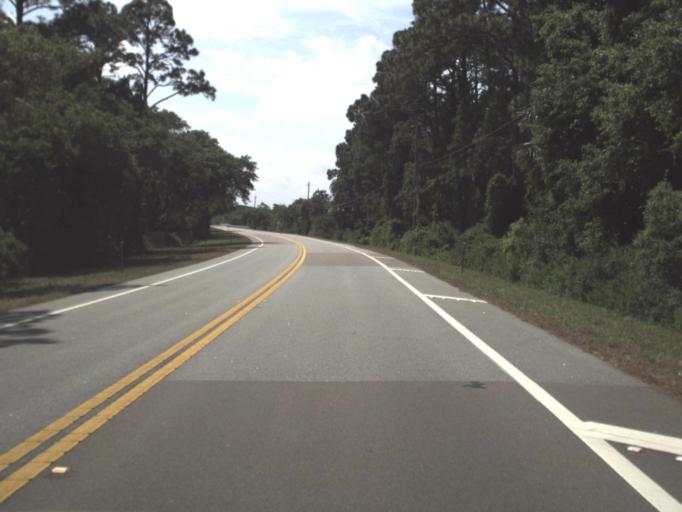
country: US
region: Florida
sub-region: Duval County
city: Atlantic Beach
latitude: 30.4601
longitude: -81.4211
